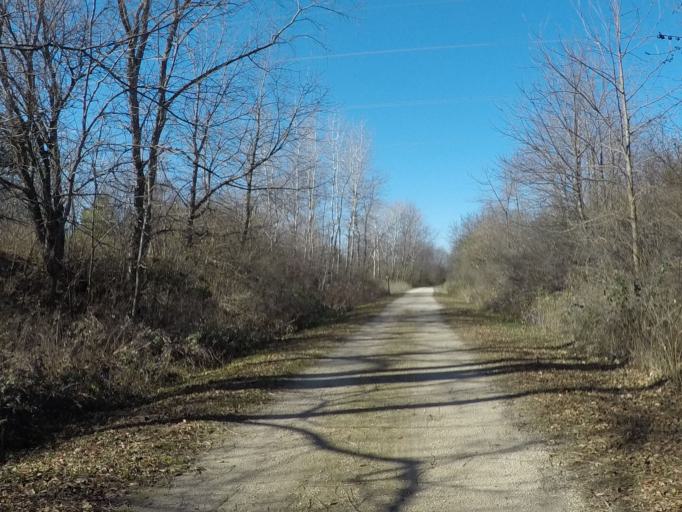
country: US
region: Wisconsin
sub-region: Dane County
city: Deerfield
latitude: 43.0422
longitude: -89.0411
